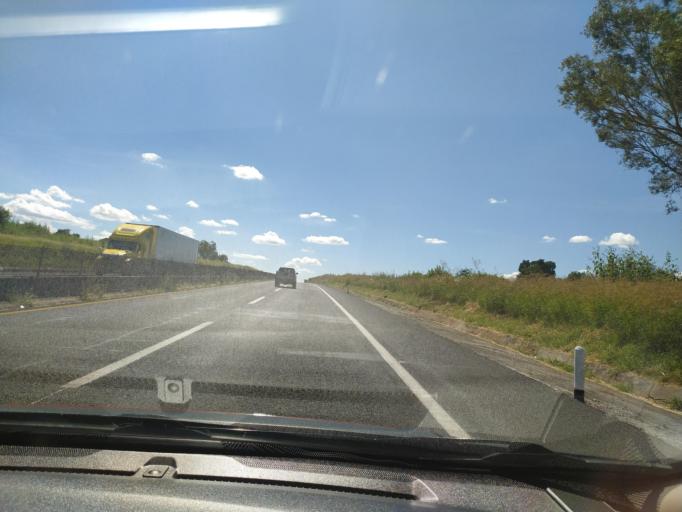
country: MX
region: Jalisco
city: Zapotlanejo
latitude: 20.6515
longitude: -103.0664
